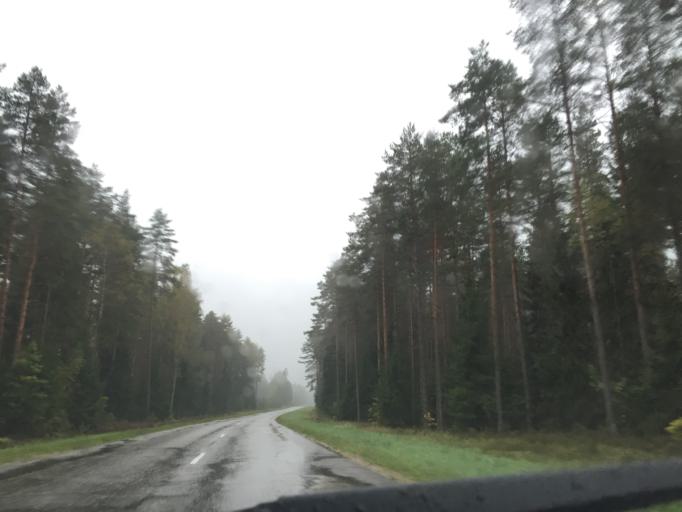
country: LV
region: Ropazu
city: Ropazi
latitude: 57.0208
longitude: 24.6835
